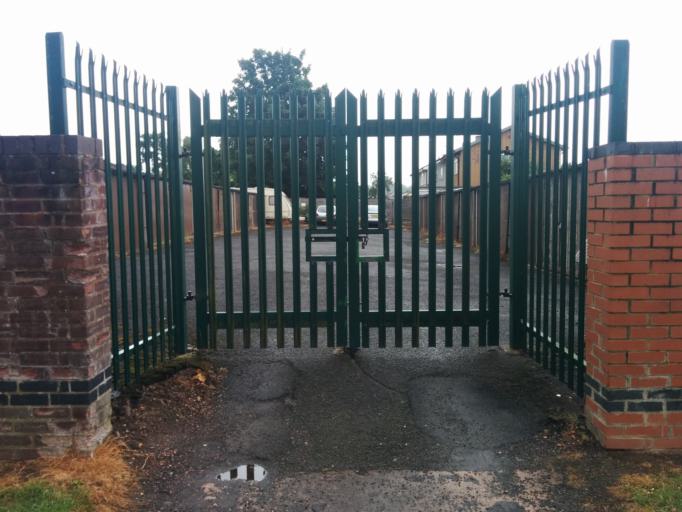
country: GB
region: England
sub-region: Warwickshire
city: Kenilworth
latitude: 52.3937
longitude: -1.5763
